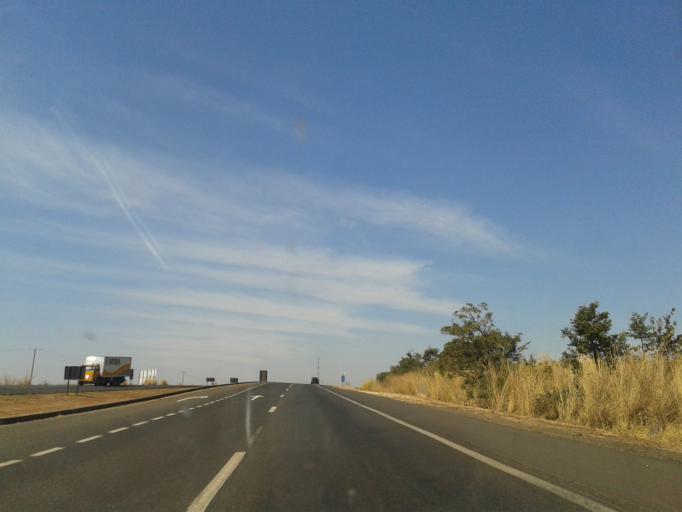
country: BR
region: Minas Gerais
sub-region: Monte Alegre De Minas
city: Monte Alegre de Minas
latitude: -18.8571
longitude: -49.0785
